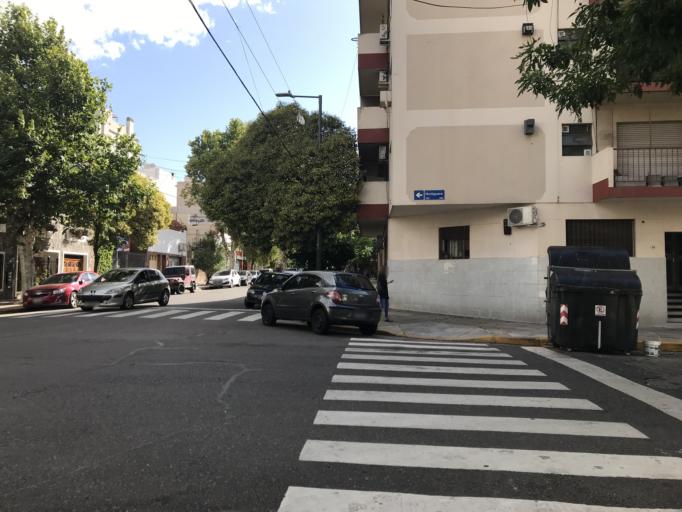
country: AR
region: Buenos Aires F.D.
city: Villa Santa Rita
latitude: -34.6305
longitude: -58.4440
